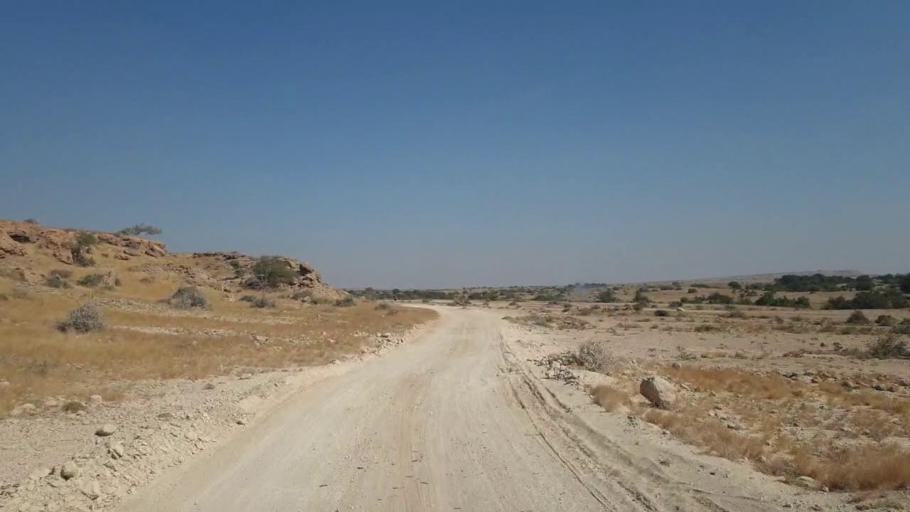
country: PK
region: Sindh
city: Thatta
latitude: 25.2208
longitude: 67.7988
